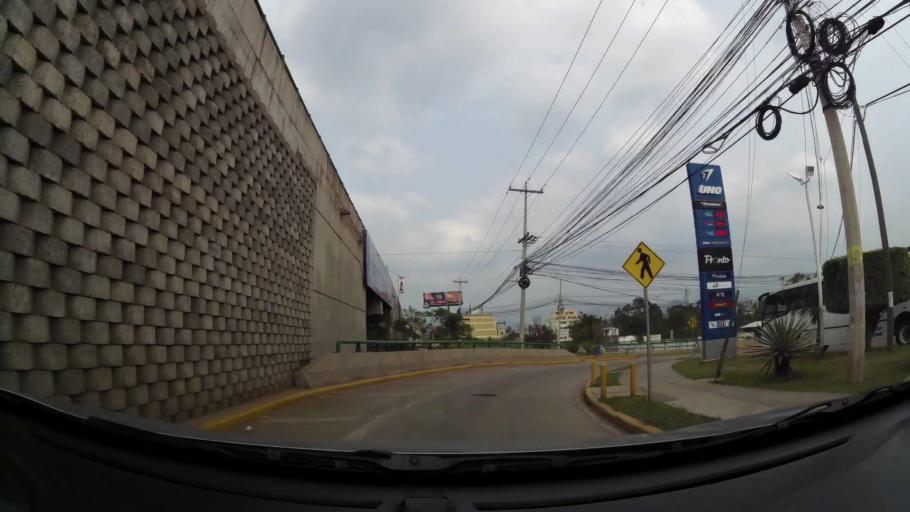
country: HN
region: Francisco Morazan
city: Tegucigalpa
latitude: 14.0841
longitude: -87.1734
